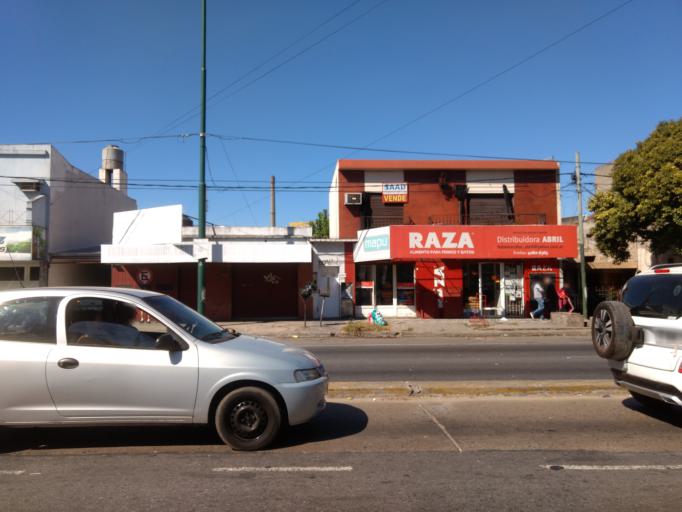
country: AR
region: Buenos Aires
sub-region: Partido de Lomas de Zamora
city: Lomas de Zamora
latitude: -34.7682
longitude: -58.4380
